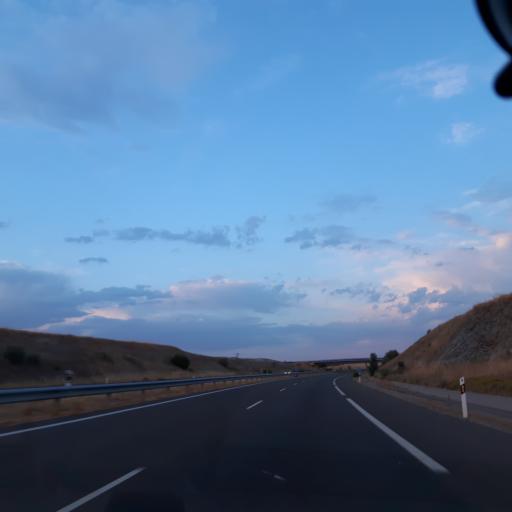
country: ES
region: Castille and Leon
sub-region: Provincia de Salamanca
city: Mozarbez
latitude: 40.8590
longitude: -5.6421
